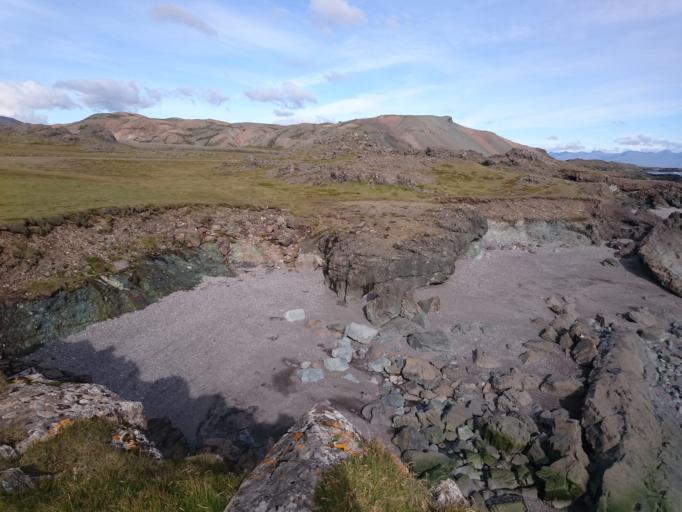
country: IS
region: East
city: Reydarfjoerdur
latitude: 64.4765
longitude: -14.4902
